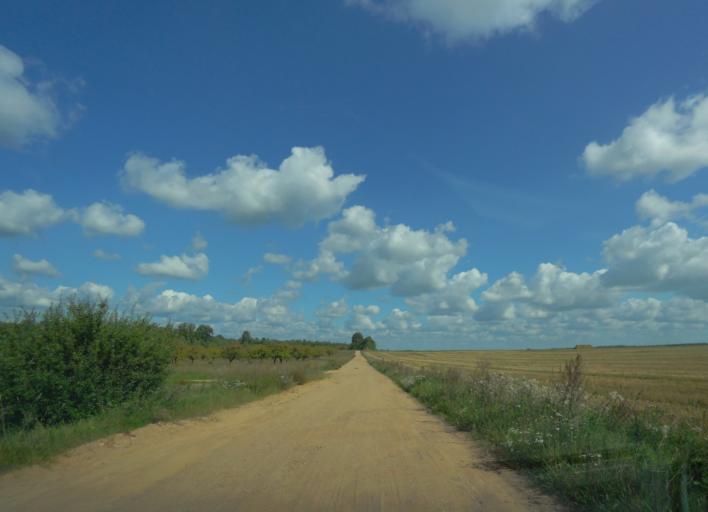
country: BY
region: Minsk
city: Zyembin
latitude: 54.3767
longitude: 28.3454
